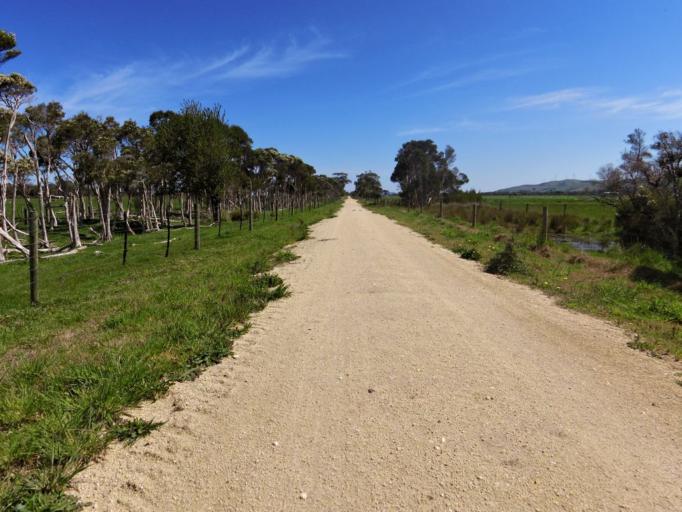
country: AU
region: Victoria
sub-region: Latrobe
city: Morwell
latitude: -38.6678
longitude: 146.4295
